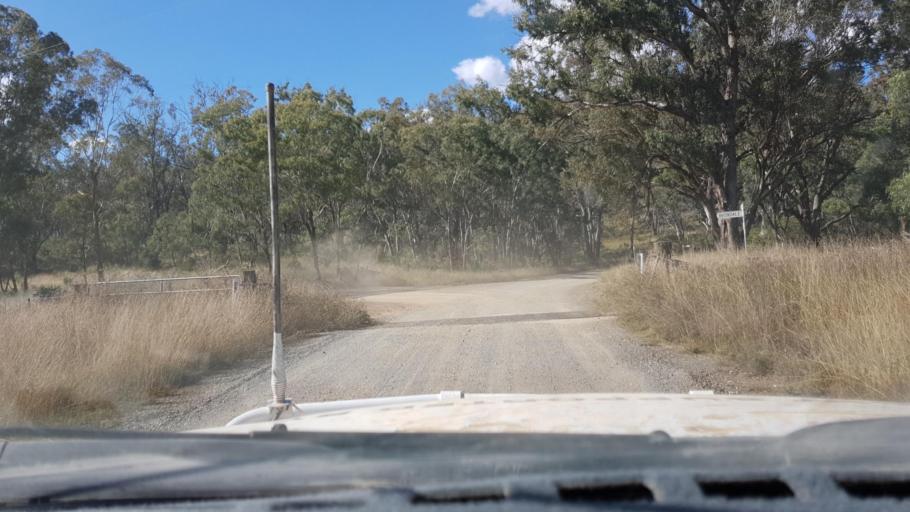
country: AU
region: New South Wales
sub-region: Tamworth Municipality
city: Manilla
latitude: -30.4810
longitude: 150.7675
